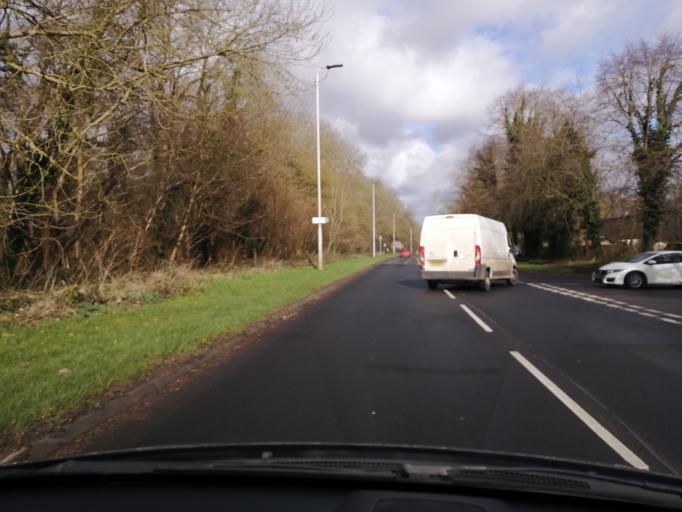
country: GB
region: England
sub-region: Peterborough
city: Marholm
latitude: 52.5943
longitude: -0.2879
